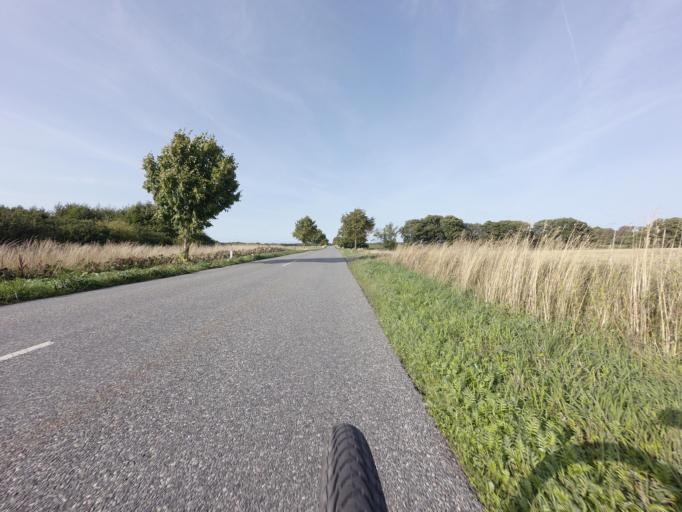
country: DK
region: Zealand
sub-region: Faxe Kommune
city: Fakse Ladeplads
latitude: 55.2400
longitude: 12.2162
